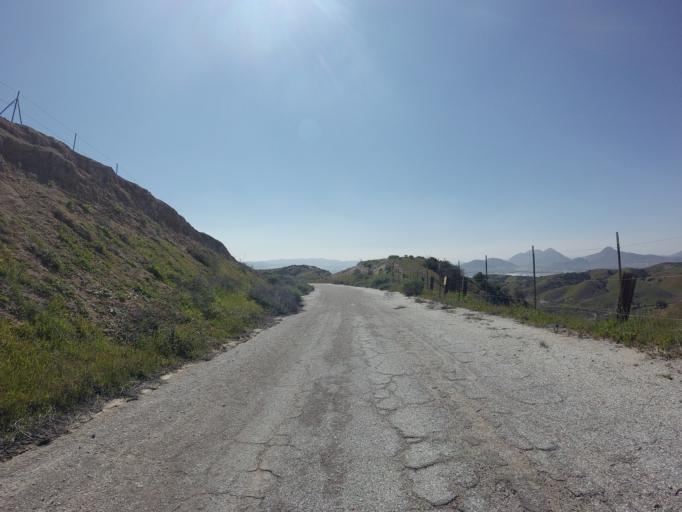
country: US
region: California
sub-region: Riverside County
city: Beaumont
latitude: 33.9059
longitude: -117.0610
